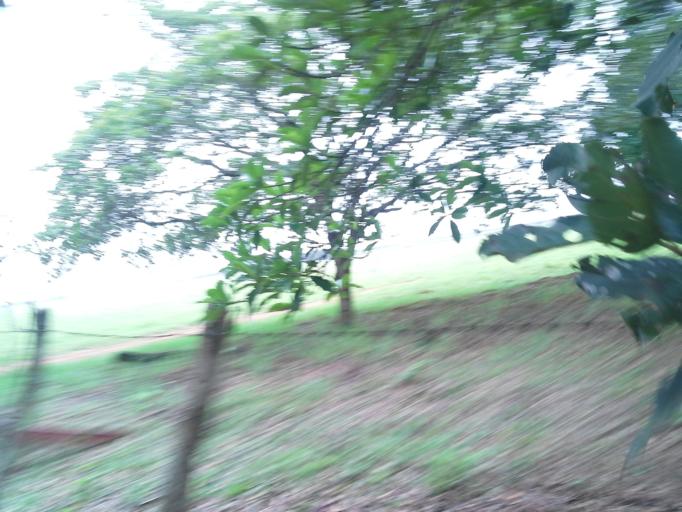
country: CO
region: Cundinamarca
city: Tibacuy
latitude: 4.1913
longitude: -72.4323
